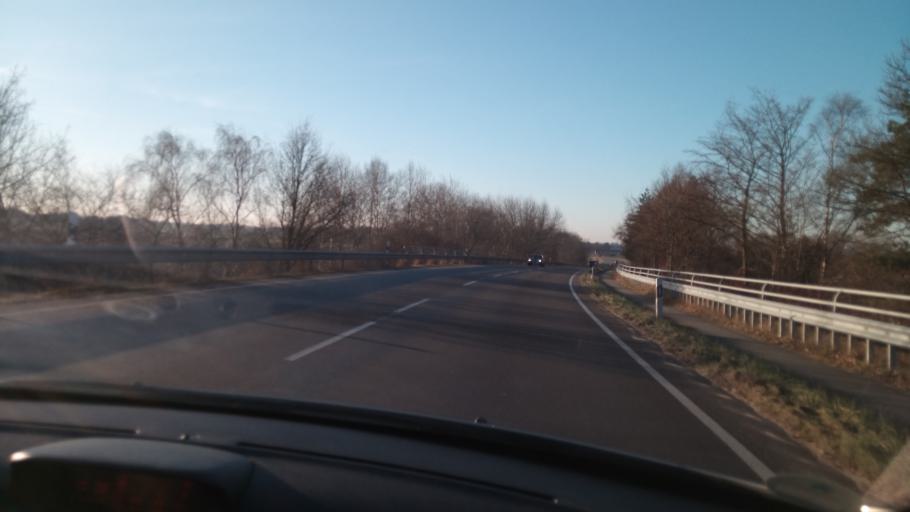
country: DE
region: Lower Saxony
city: Artlenburg
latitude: 53.3683
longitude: 10.5000
